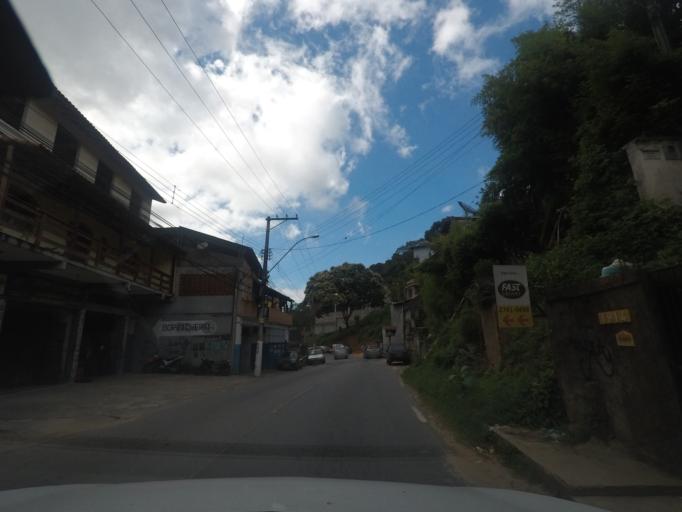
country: BR
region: Rio de Janeiro
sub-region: Teresopolis
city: Teresopolis
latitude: -22.3878
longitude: -42.9544
